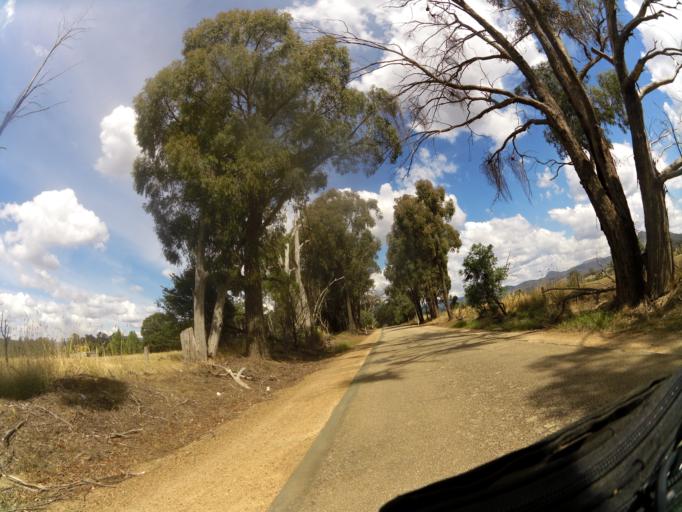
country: AU
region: Victoria
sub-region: Benalla
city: Benalla
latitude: -36.7622
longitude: 145.9769
